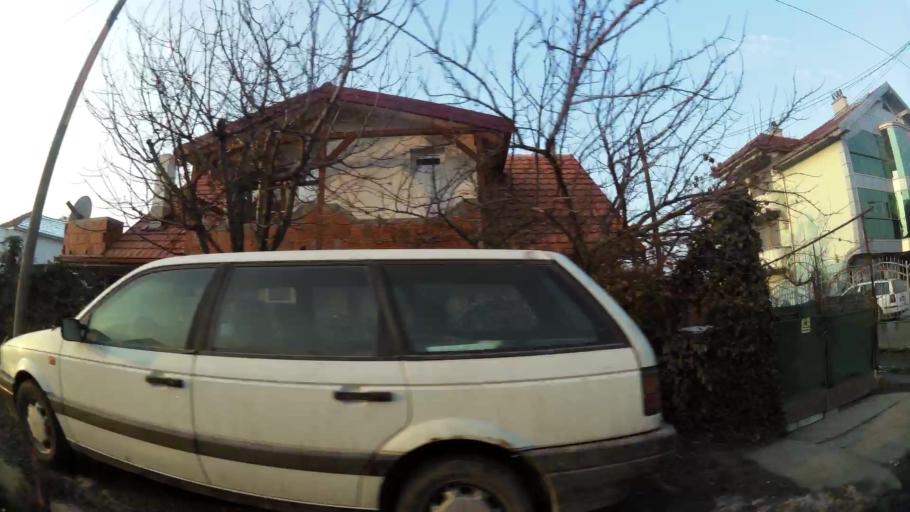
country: MK
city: Creshevo
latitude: 42.0139
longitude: 21.5186
